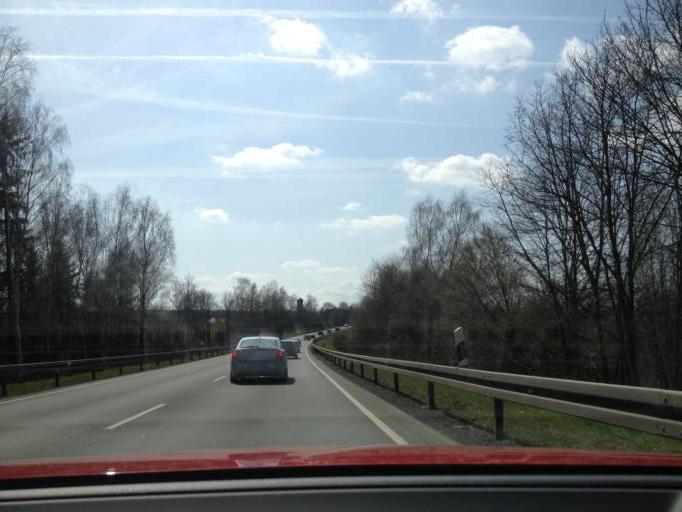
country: DE
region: Bavaria
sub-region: Upper Franconia
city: Arzberg
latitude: 50.0398
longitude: 12.1600
